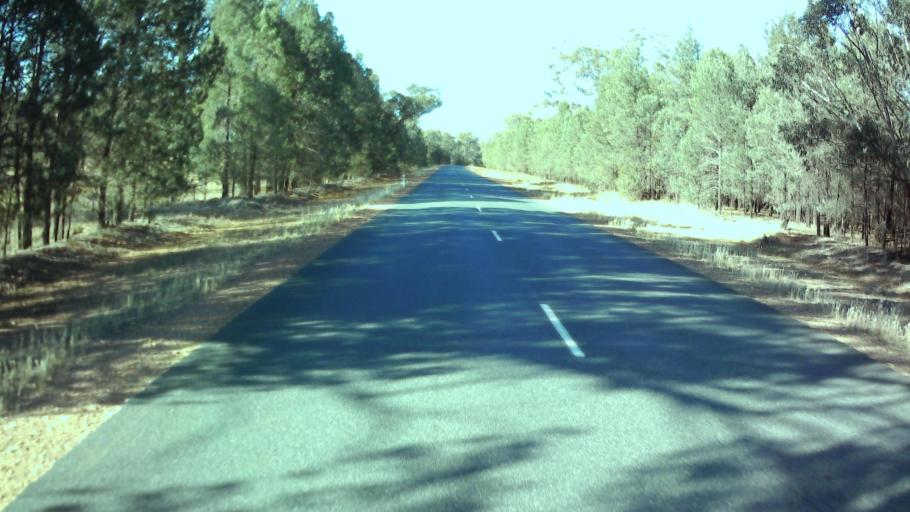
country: AU
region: New South Wales
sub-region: Weddin
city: Grenfell
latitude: -34.0276
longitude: 148.0958
